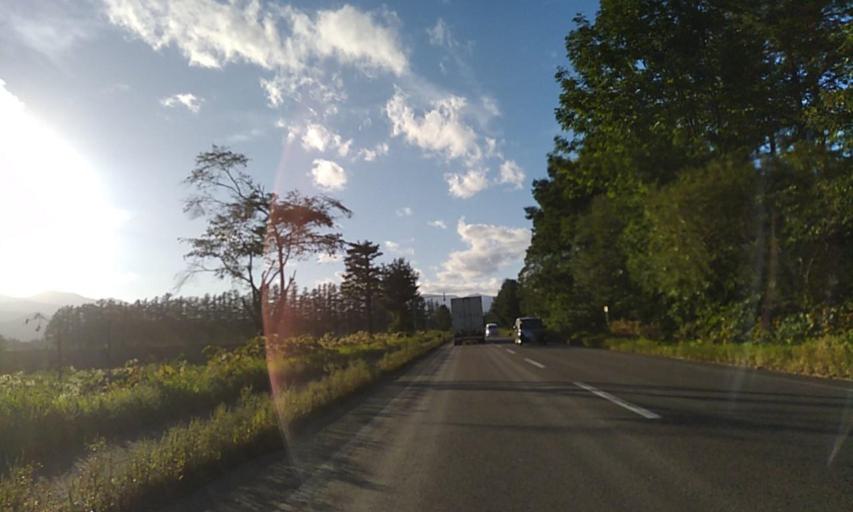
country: JP
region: Hokkaido
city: Otofuke
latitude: 42.9559
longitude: 142.9172
